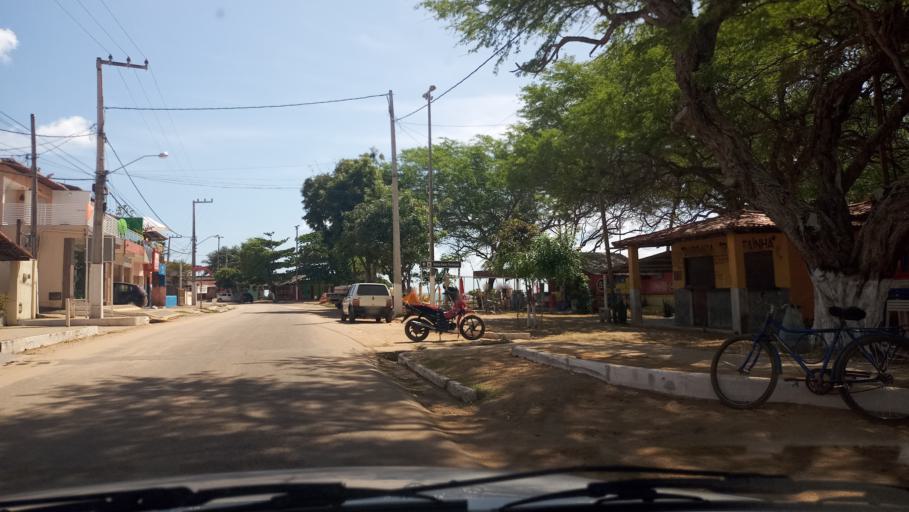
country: BR
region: Rio Grande do Norte
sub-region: Canguaretama
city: Canguaretama
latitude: -6.3149
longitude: -35.0431
